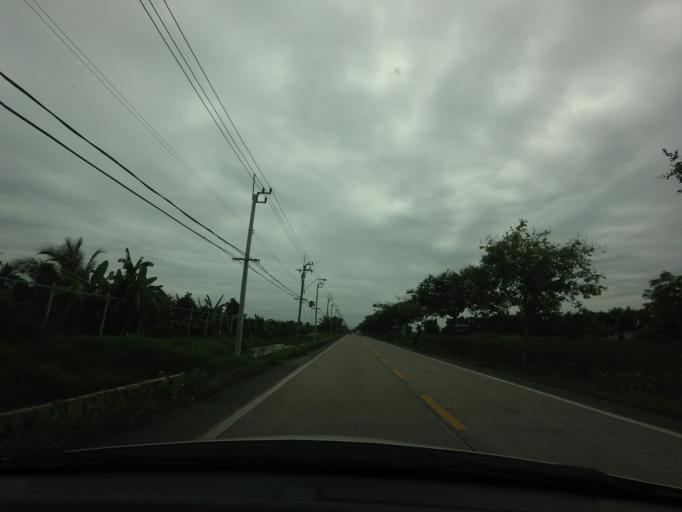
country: TH
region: Pathum Thani
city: Lam Luk Ka
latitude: 13.9190
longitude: 100.7878
